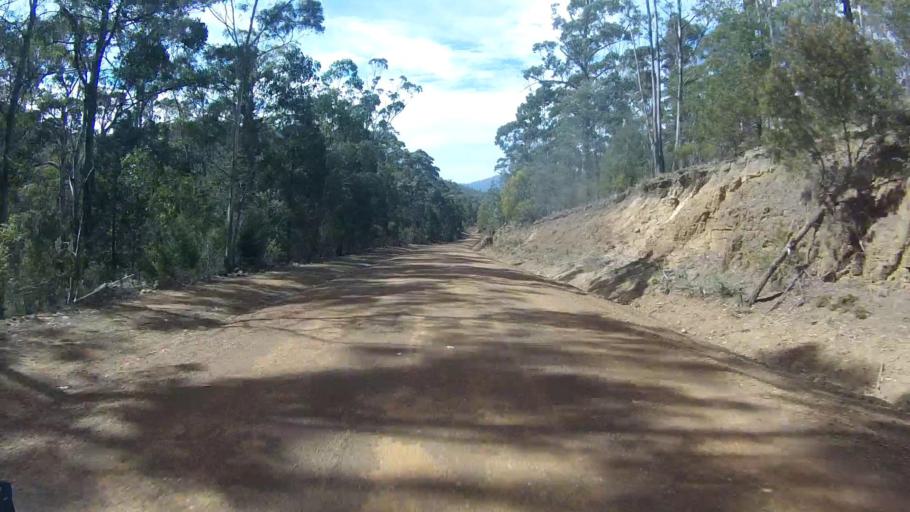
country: AU
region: Tasmania
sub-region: Sorell
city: Sorell
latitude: -42.6142
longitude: 147.8987
